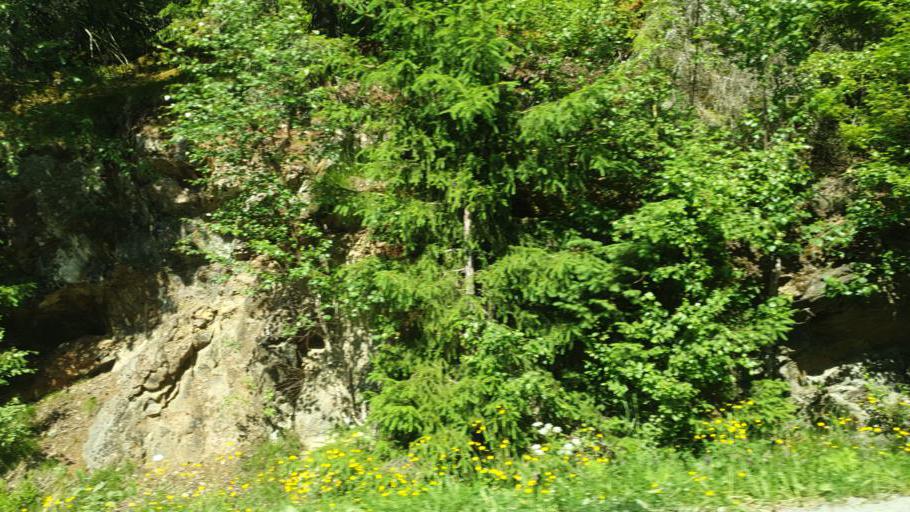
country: NO
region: Nord-Trondelag
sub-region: Leksvik
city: Leksvik
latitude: 63.6808
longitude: 10.6636
